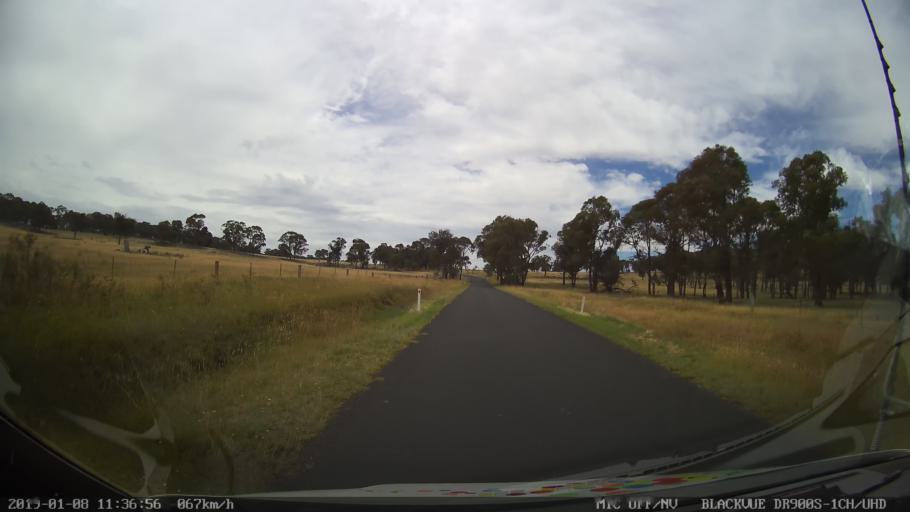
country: AU
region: New South Wales
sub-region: Guyra
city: Guyra
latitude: -30.3487
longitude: 151.5478
